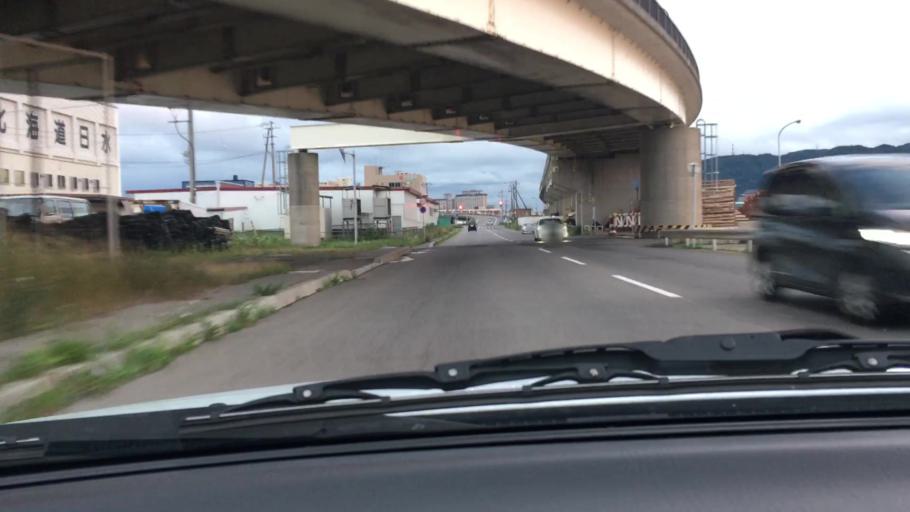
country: JP
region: Hokkaido
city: Hakodate
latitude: 41.7851
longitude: 140.7271
